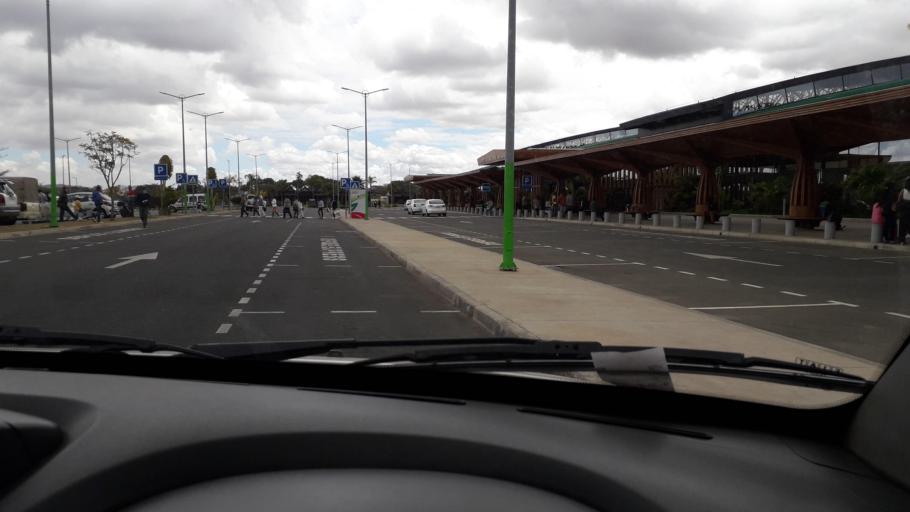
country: MG
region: Analamanga
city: Antananarivo
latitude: -18.8014
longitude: 47.4798
